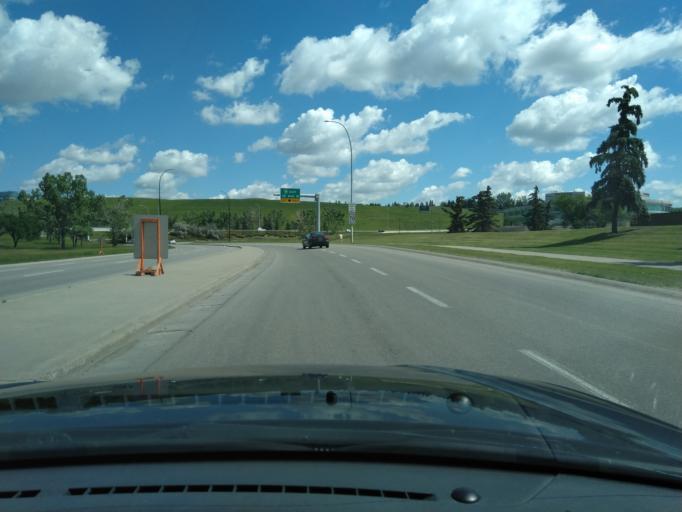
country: CA
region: Alberta
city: Calgary
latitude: 51.0639
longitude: -114.1485
